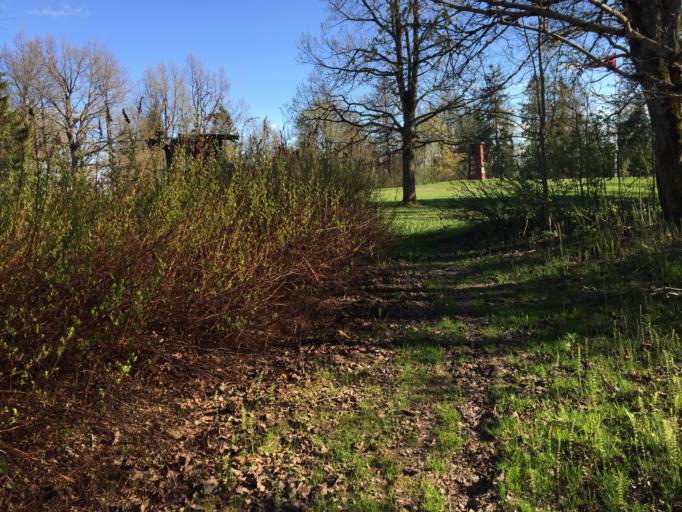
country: LV
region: Vecpiebalga
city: Vecpiebalga
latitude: 56.8708
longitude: 25.9596
